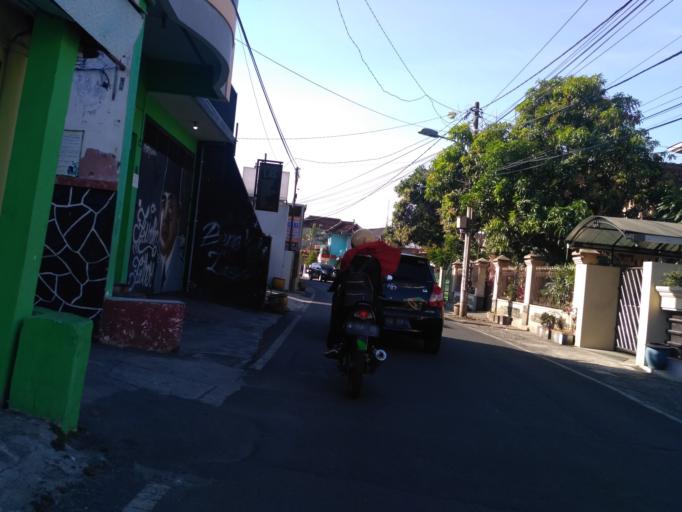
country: ID
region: East Java
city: Malang
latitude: -7.9377
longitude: 112.6022
